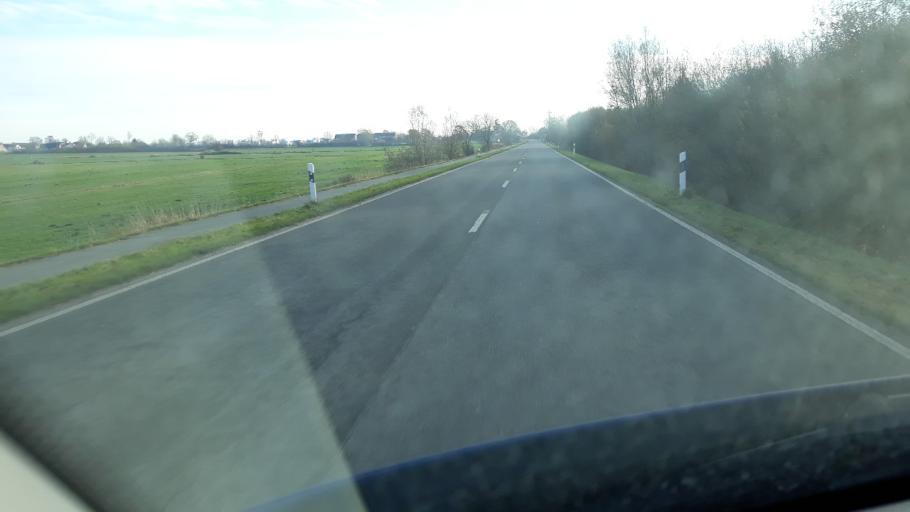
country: DE
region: Schleswig-Holstein
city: Maasholm
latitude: 54.6607
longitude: 9.9970
